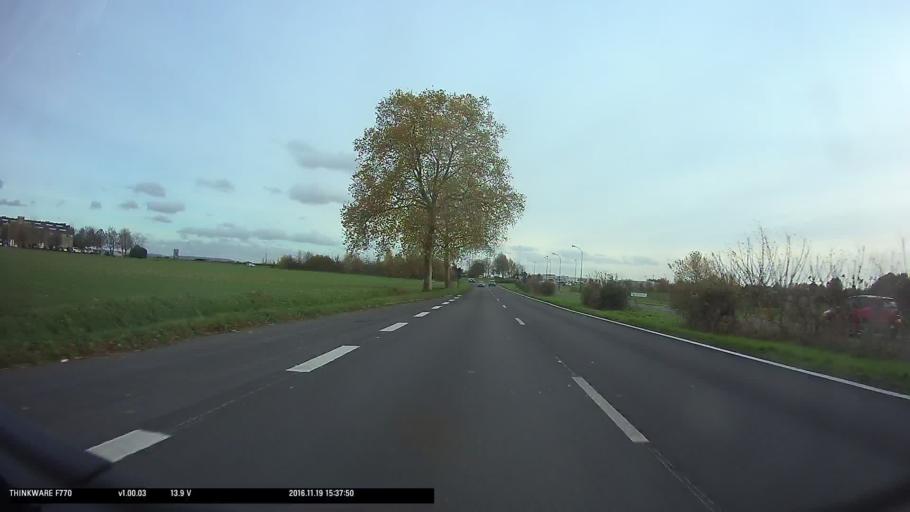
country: FR
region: Ile-de-France
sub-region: Departement du Val-d'Oise
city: Osny
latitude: 49.0815
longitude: 2.0698
